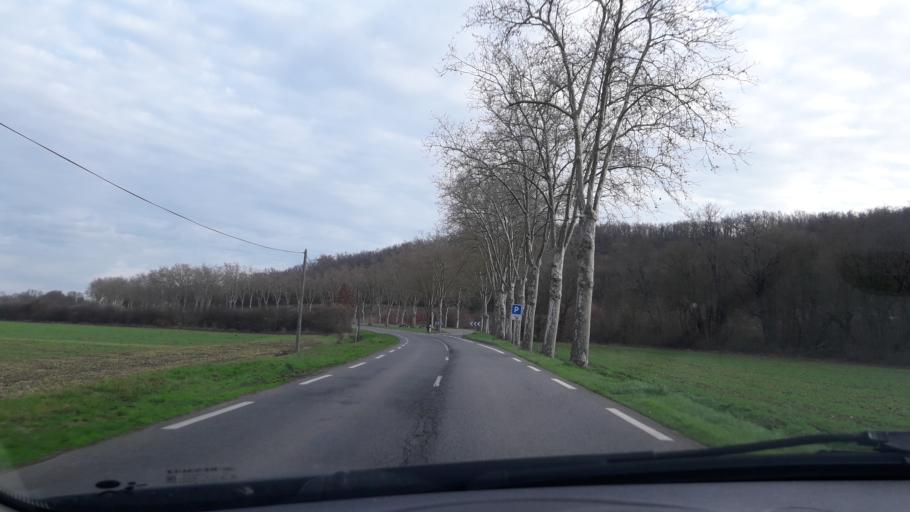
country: FR
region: Midi-Pyrenees
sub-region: Departement de la Haute-Garonne
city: Grenade
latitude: 43.7401
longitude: 1.2634
